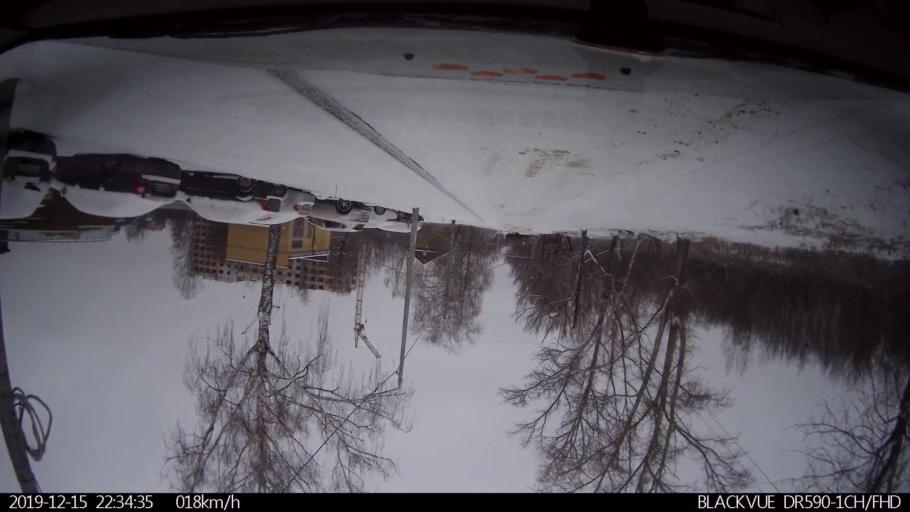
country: RU
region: Nizjnij Novgorod
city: Gorbatovka
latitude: 56.3427
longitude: 43.8303
